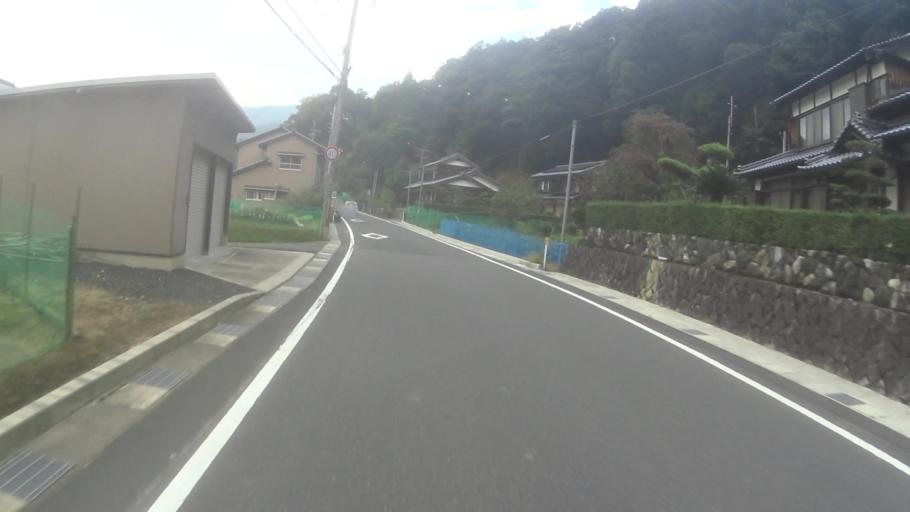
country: JP
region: Kyoto
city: Miyazu
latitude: 35.5018
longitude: 135.1768
